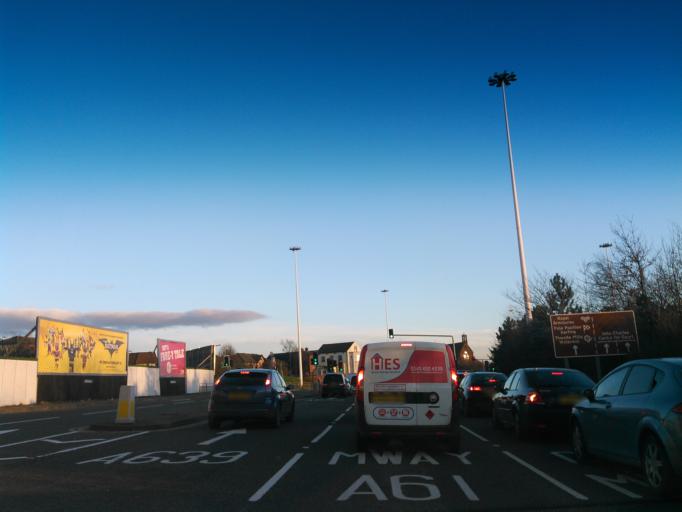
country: GB
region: England
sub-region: City and Borough of Leeds
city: Leeds
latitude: 53.7902
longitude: -1.5254
